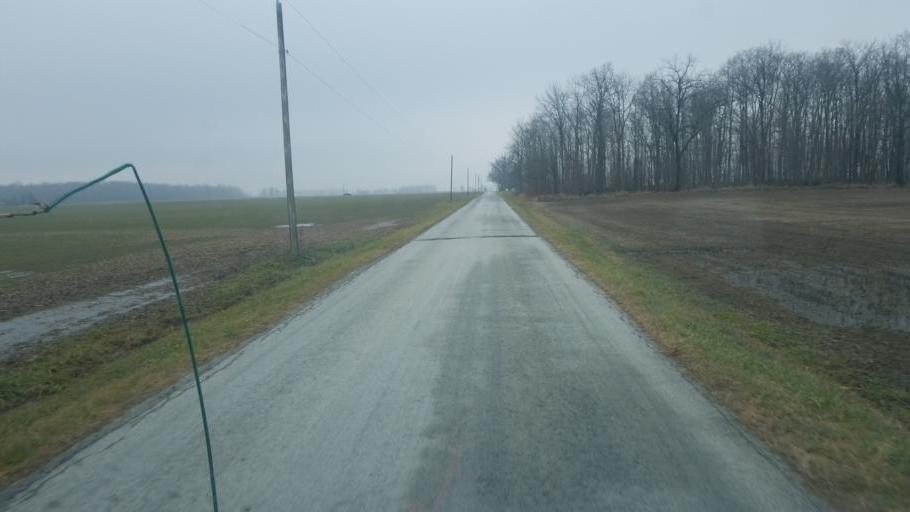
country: US
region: Ohio
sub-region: Hardin County
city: Kenton
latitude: 40.6676
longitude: -83.4775
